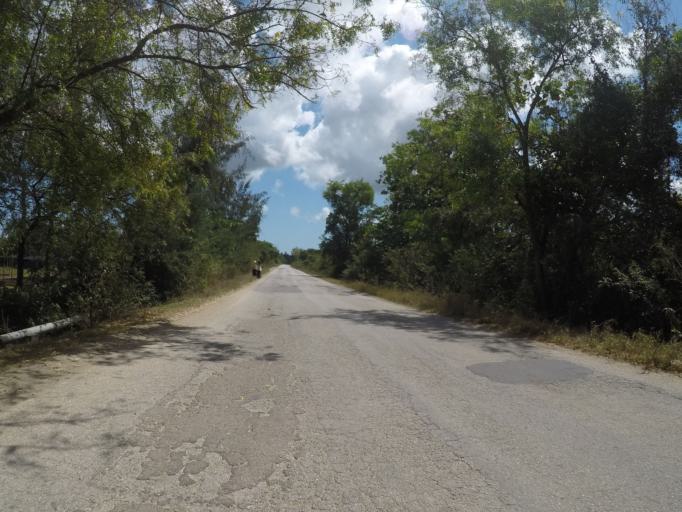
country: TZ
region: Zanzibar Central/South
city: Nganane
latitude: -6.2874
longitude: 39.4453
